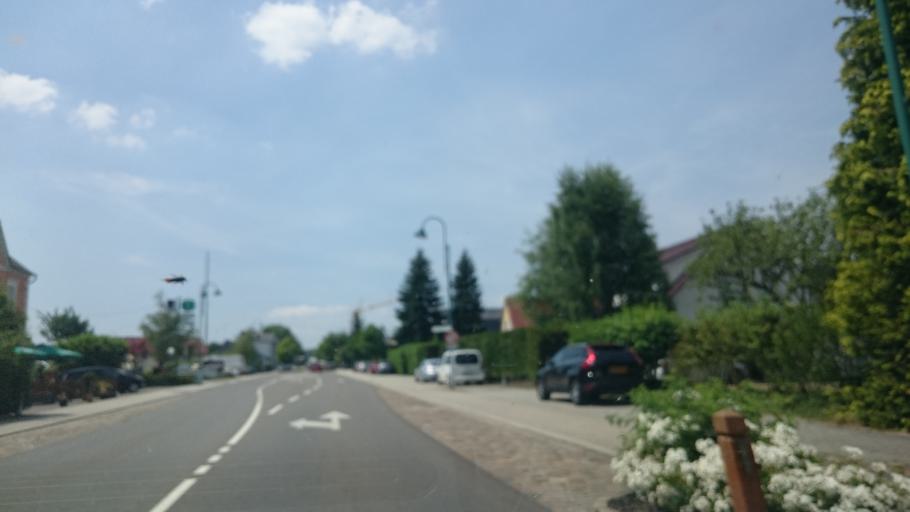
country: LU
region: Luxembourg
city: Capellen
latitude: 49.6437
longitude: 5.9943
